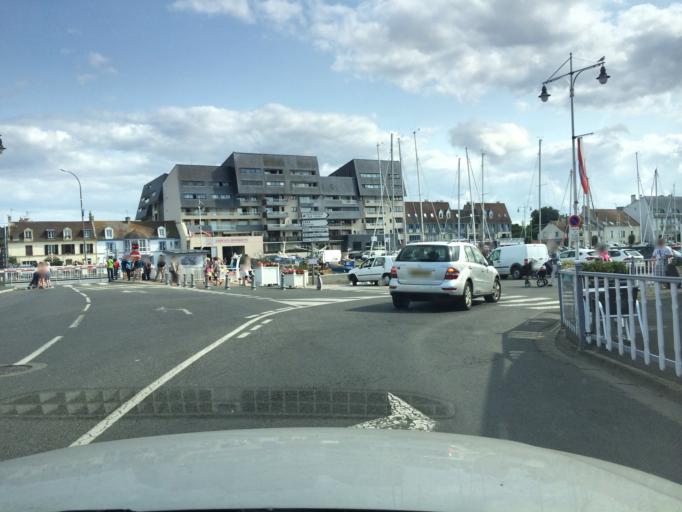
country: FR
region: Lower Normandy
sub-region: Departement du Calvados
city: Courseulles-sur-Mer
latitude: 49.3341
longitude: -0.4623
